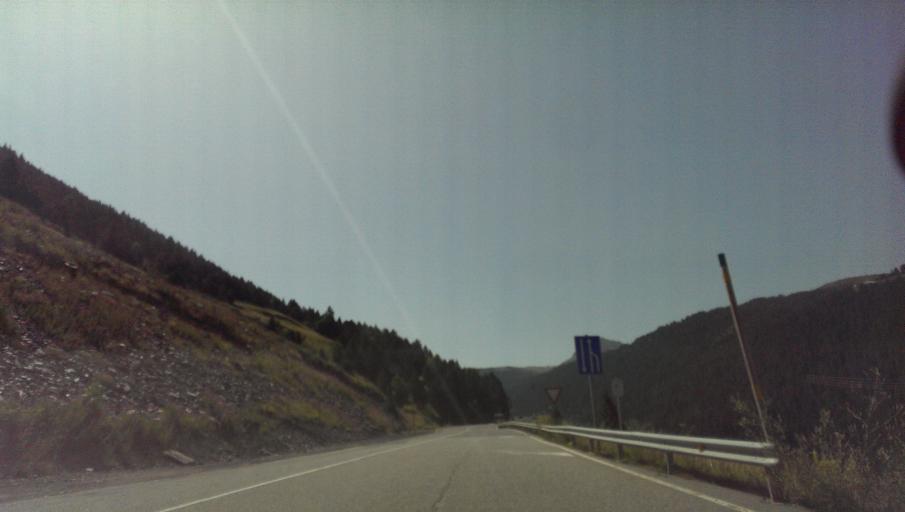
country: AD
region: Canillo
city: El Tarter
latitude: 42.5696
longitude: 1.6783
